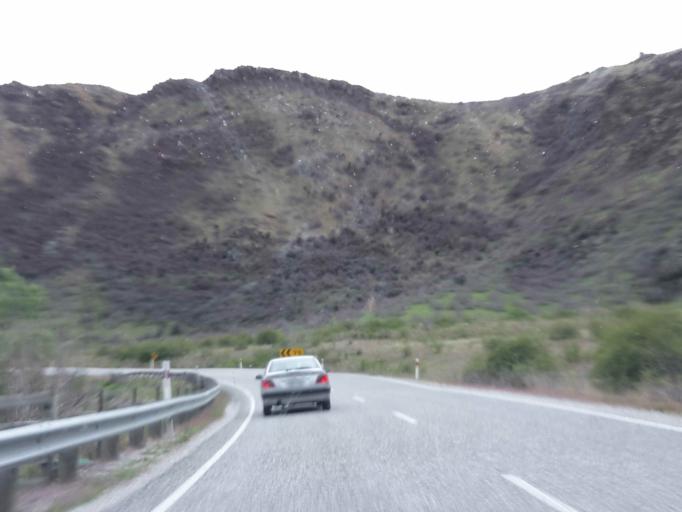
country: NZ
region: Otago
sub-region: Queenstown-Lakes District
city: Wanaka
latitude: -44.7340
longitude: 169.5082
